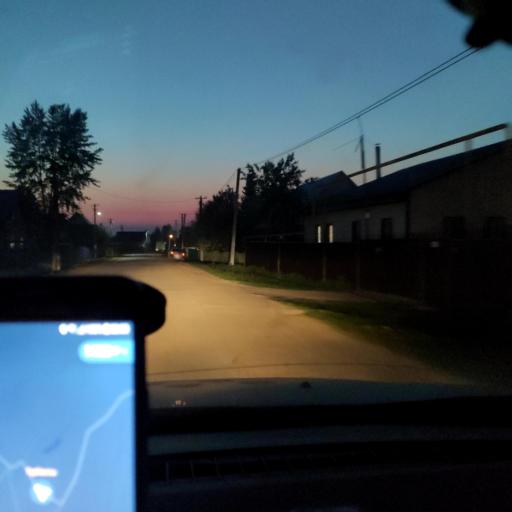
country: RU
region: Bashkortostan
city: Kabakovo
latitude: 54.6521
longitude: 56.3058
